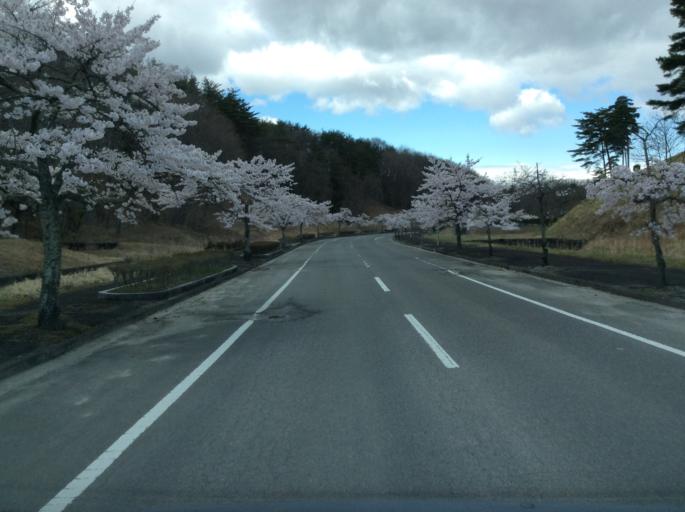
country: JP
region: Fukushima
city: Koriyama
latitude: 37.3510
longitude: 140.4369
